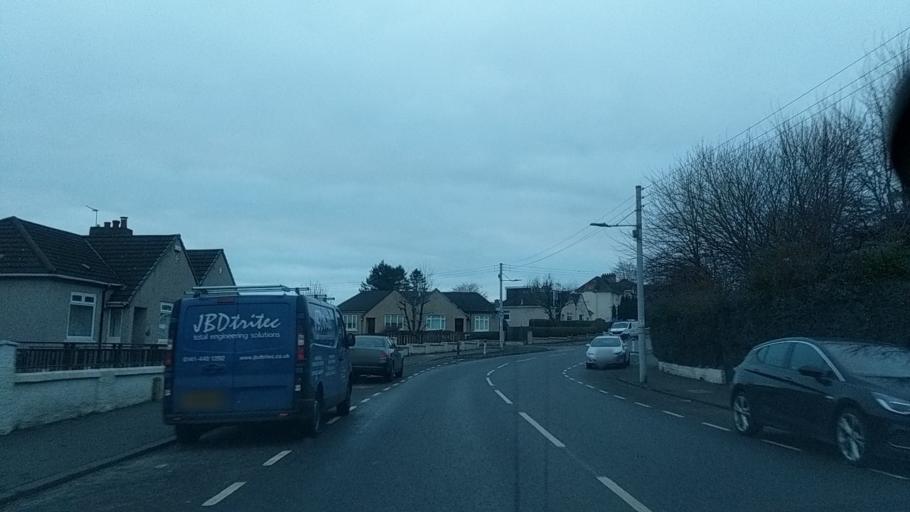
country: GB
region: Scotland
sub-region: South Lanarkshire
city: Rutherglen
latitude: 55.8265
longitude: -4.1968
